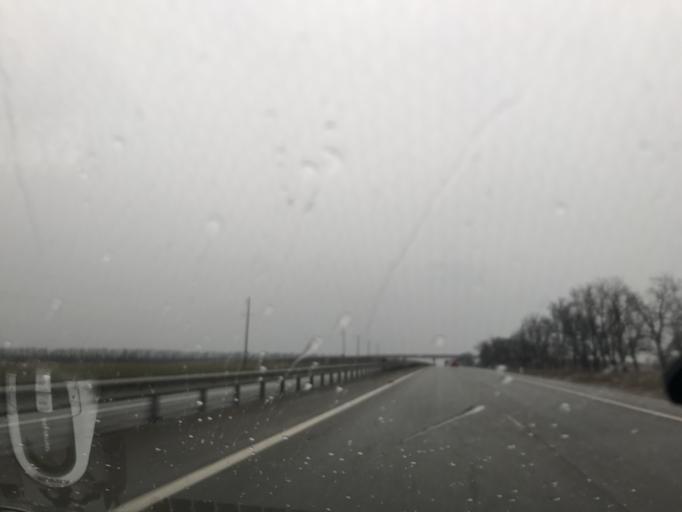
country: RU
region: Krasnodarskiy
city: Kislyakovskaya
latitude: 46.3551
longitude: 39.7681
